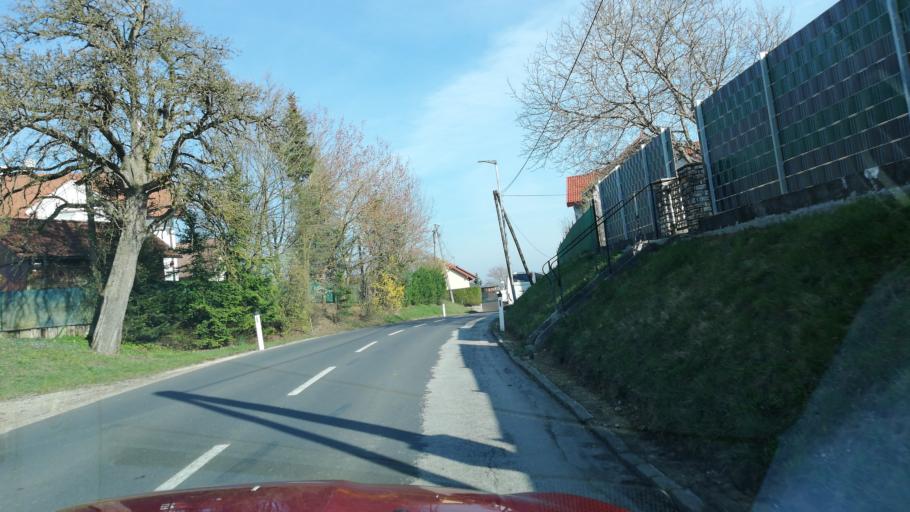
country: AT
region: Upper Austria
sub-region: Politischer Bezirk Kirchdorf an der Krems
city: Kremsmunster
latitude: 48.0650
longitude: 14.1224
